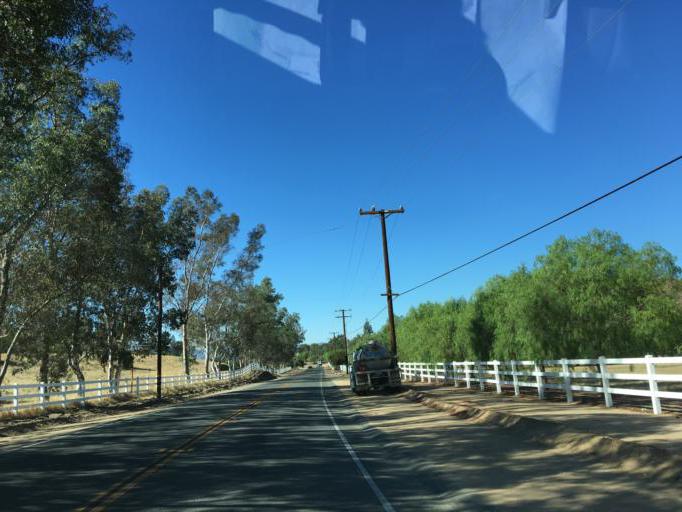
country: US
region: California
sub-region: Los Angeles County
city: Agua Dulce
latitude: 34.5161
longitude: -118.3174
